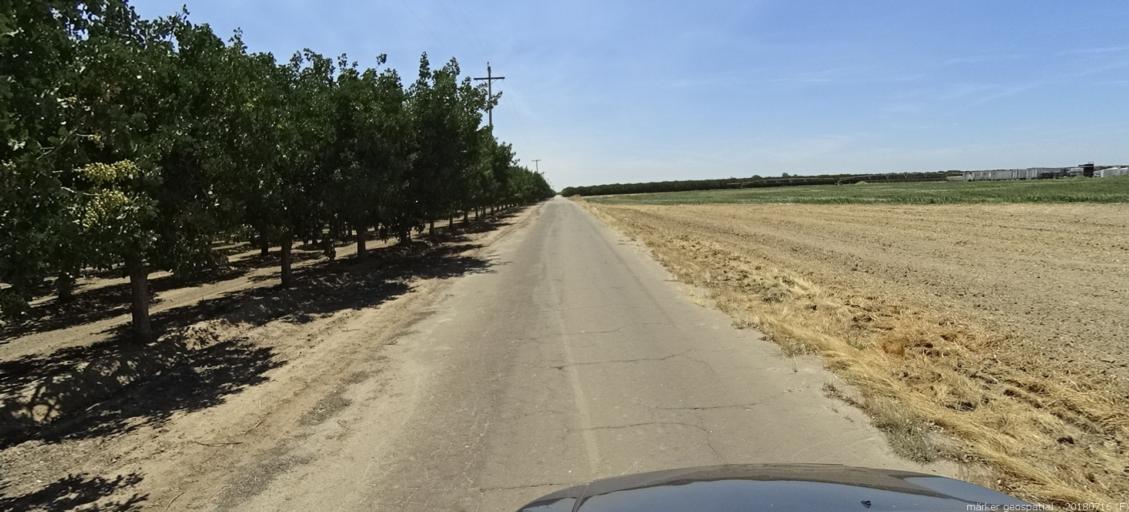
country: US
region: California
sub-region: Madera County
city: Fairmead
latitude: 37.0432
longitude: -120.1486
